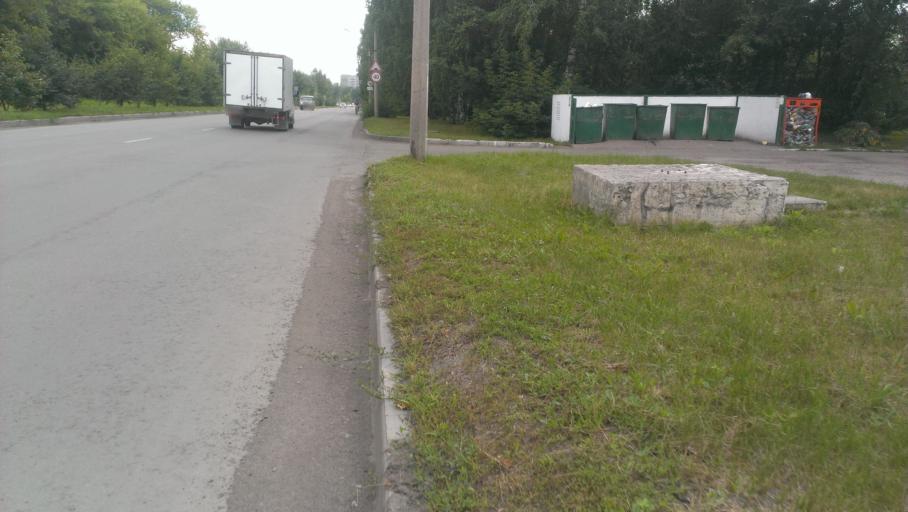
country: RU
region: Altai Krai
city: Yuzhnyy
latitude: 53.2528
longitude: 83.6972
